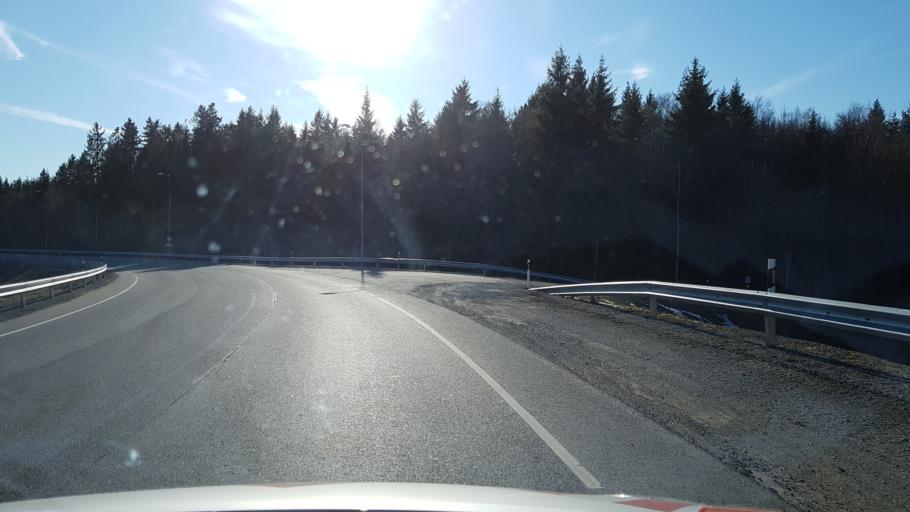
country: EE
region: Laeaene-Virumaa
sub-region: Tapa vald
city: Tapa
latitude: 59.4563
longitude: 25.9395
